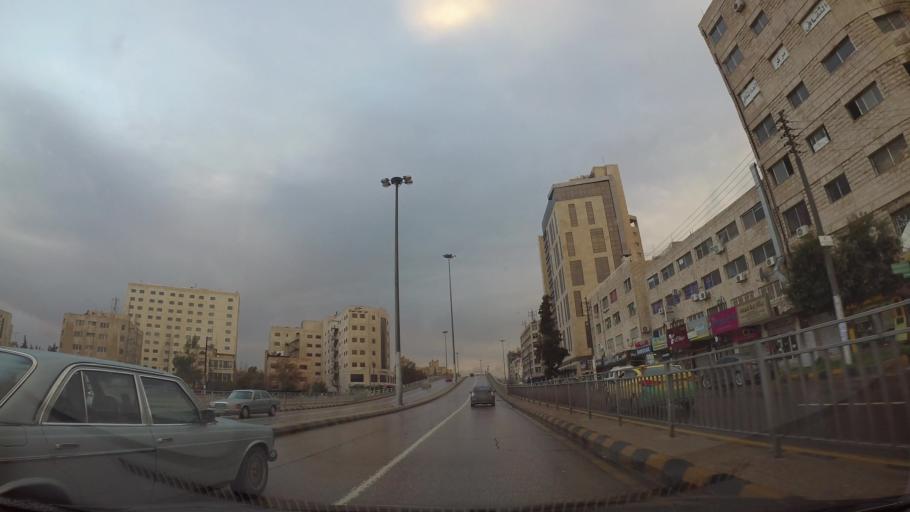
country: JO
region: Amman
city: Amman
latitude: 31.9717
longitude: 35.9119
